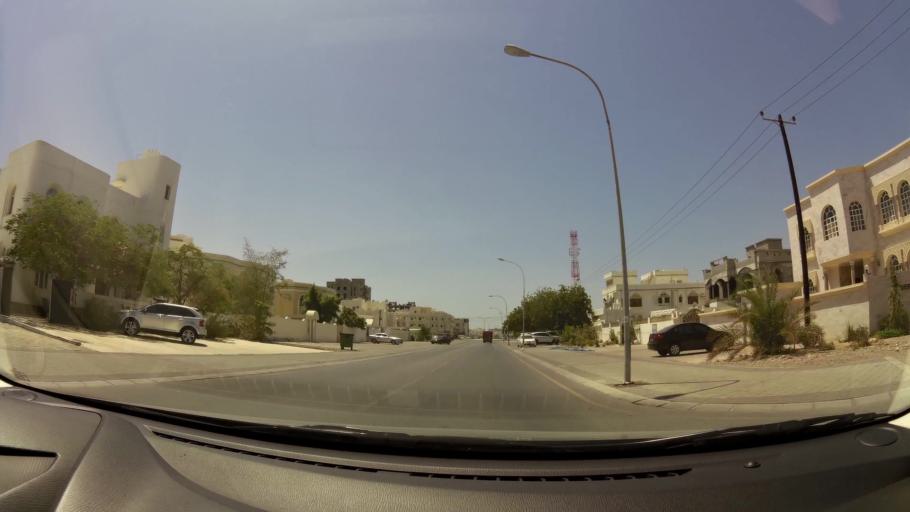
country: OM
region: Muhafazat Masqat
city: As Sib al Jadidah
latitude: 23.6244
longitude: 58.2231
